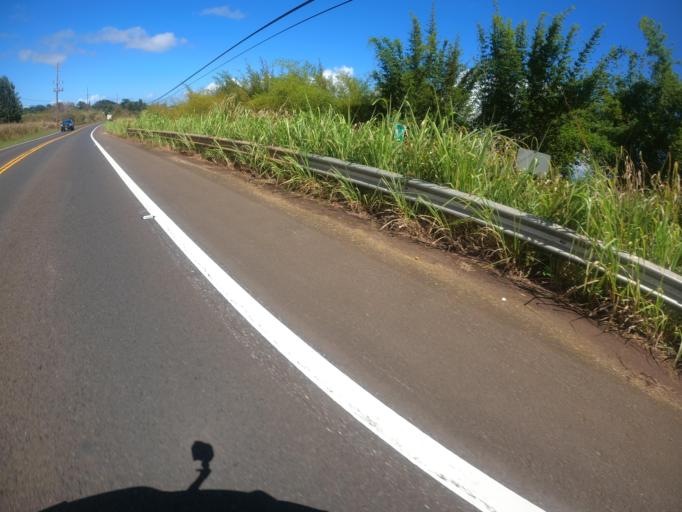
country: US
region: Hawaii
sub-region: Honolulu County
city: Schofield Barracks
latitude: 21.4509
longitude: -158.0601
